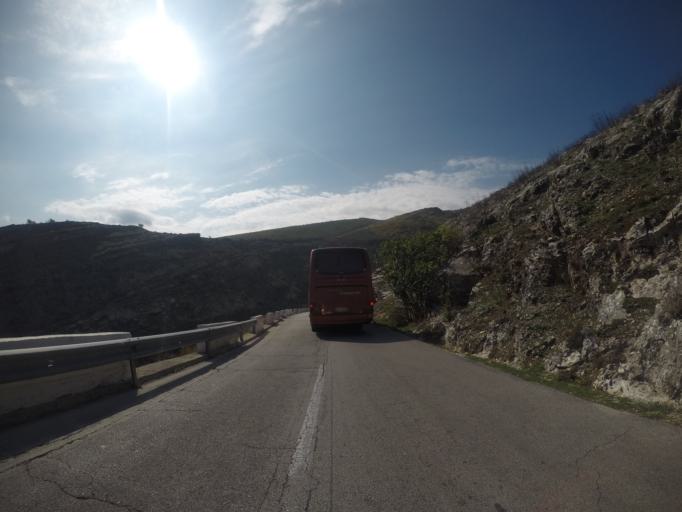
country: AL
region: Gjirokaster
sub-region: Rrethi i Gjirokastres
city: Libohove
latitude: 39.9467
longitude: 20.2510
